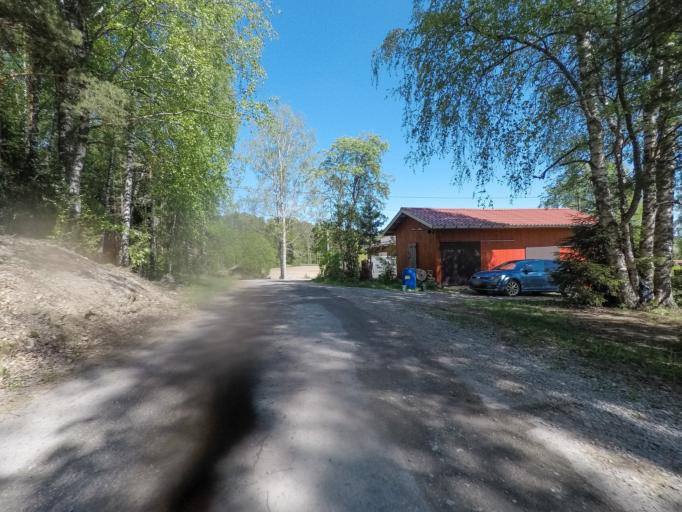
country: FI
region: Pirkanmaa
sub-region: Etelae-Pirkanmaa
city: Kylmaekoski
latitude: 61.1571
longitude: 23.7015
